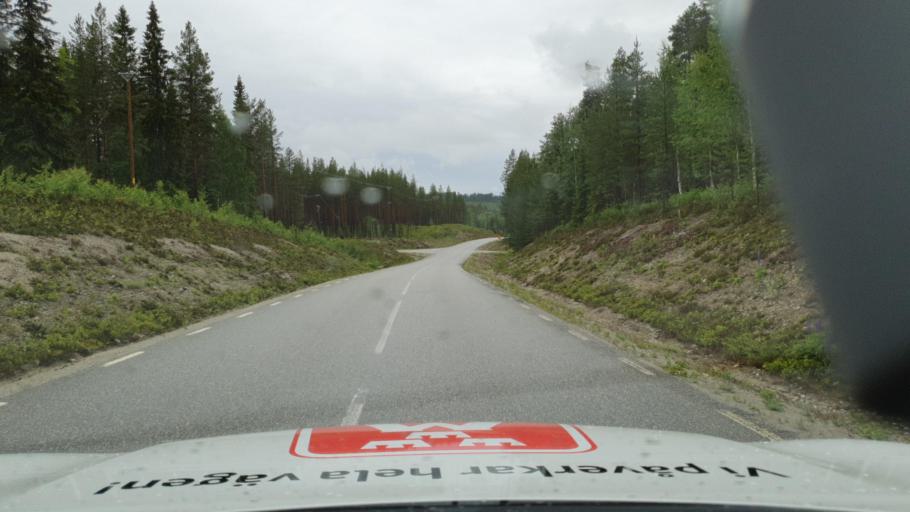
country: SE
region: Vaesterbotten
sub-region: Asele Kommun
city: Asele
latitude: 63.9858
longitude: 17.1657
